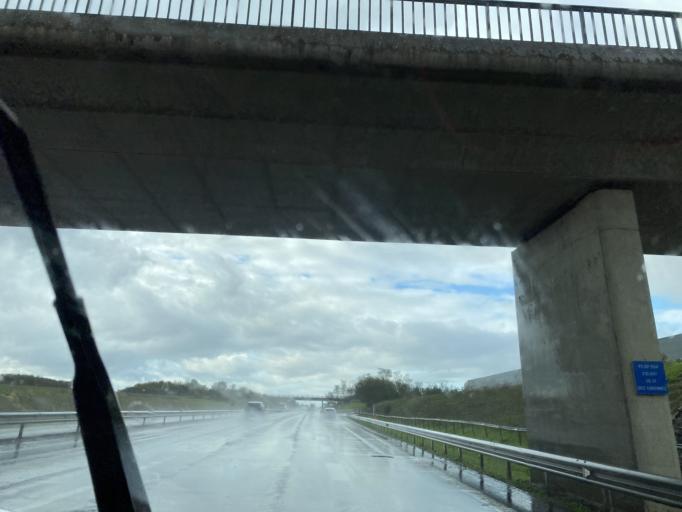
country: FR
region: Centre
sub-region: Departement du Cher
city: La Chapelle-Saint-Ursin
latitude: 47.0421
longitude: 2.3432
